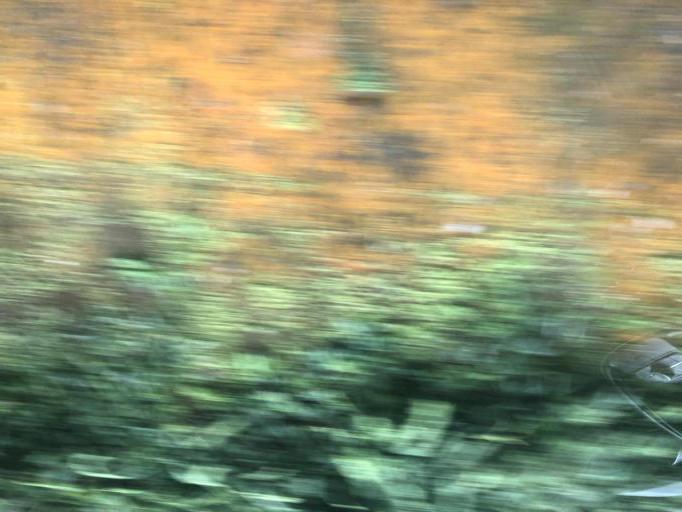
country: TW
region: Taiwan
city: Daxi
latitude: 24.8435
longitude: 121.4488
